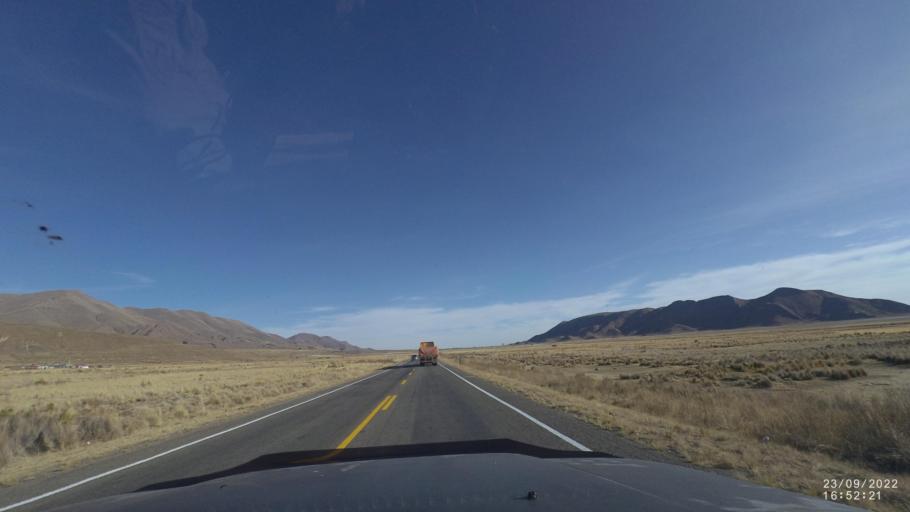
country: BO
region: Oruro
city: Poopo
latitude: -18.4301
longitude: -66.9736
